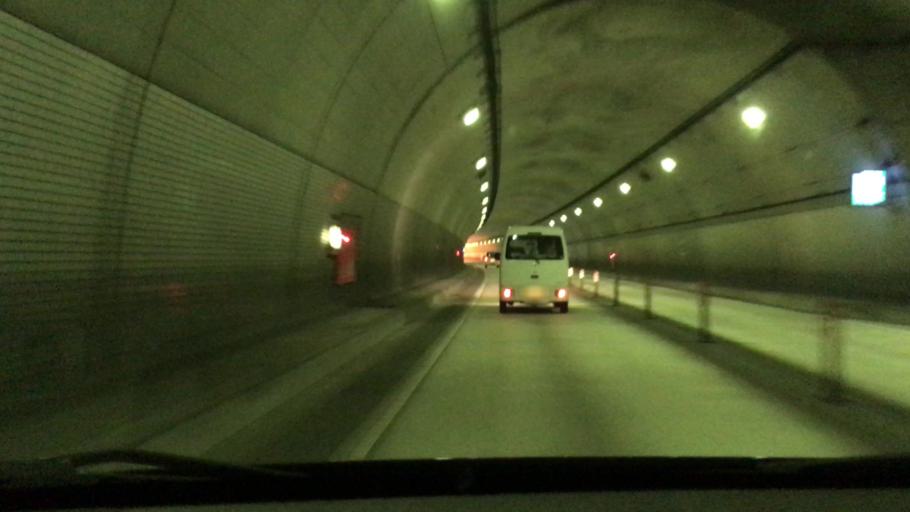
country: JP
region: Nagasaki
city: Sasebo
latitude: 33.0978
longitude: 129.7791
